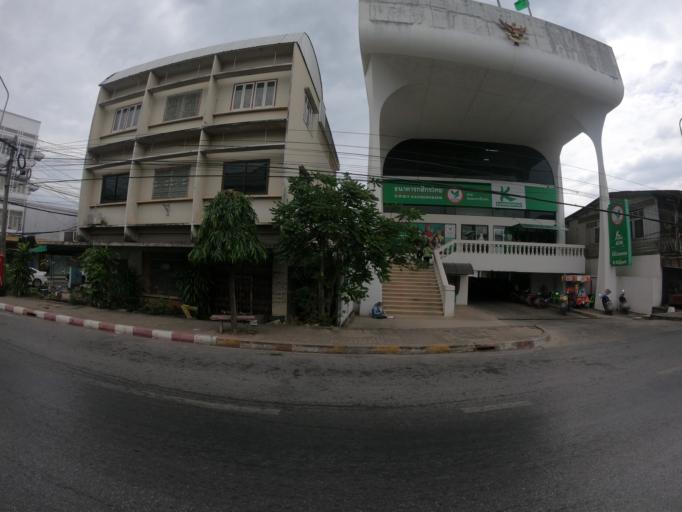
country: TH
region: Roi Et
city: Roi Et
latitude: 16.0535
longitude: 103.6480
